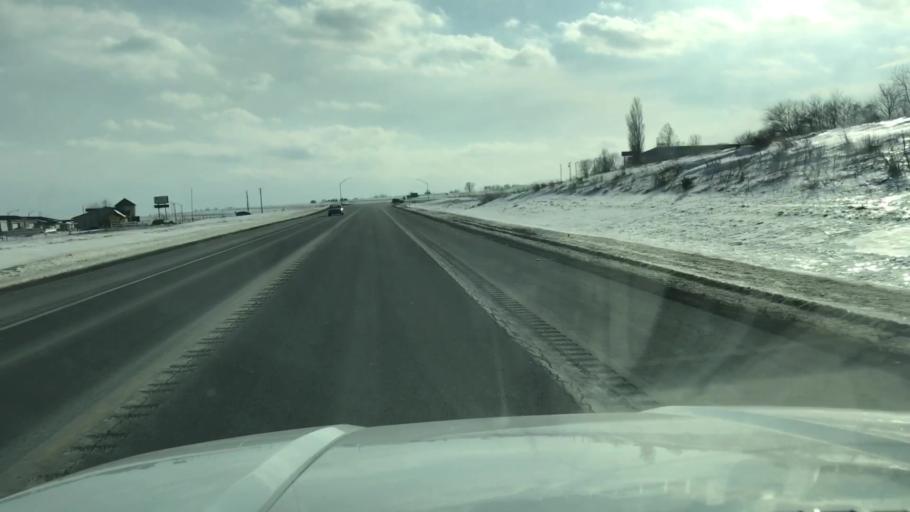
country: US
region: Missouri
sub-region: Nodaway County
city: Maryville
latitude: 40.3371
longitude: -94.8537
